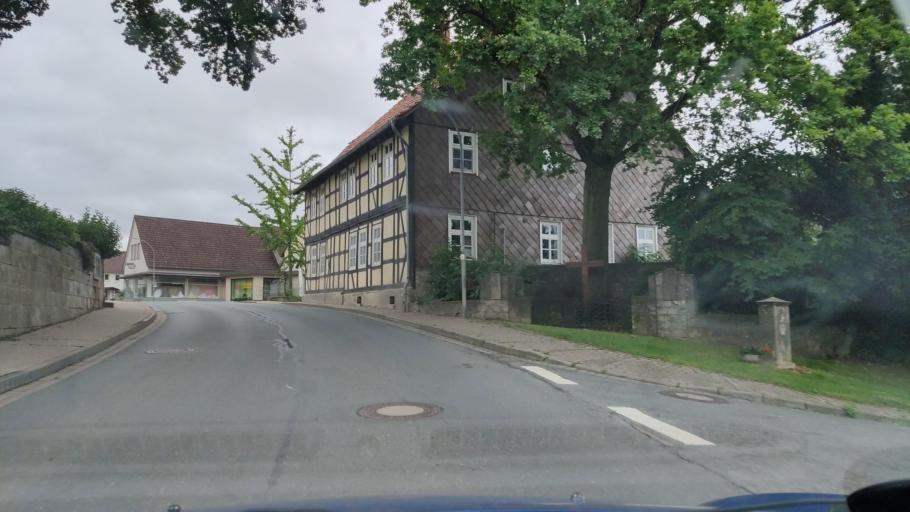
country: DE
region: Lower Saxony
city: Coppenbrugge
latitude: 52.0856
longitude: 9.5001
